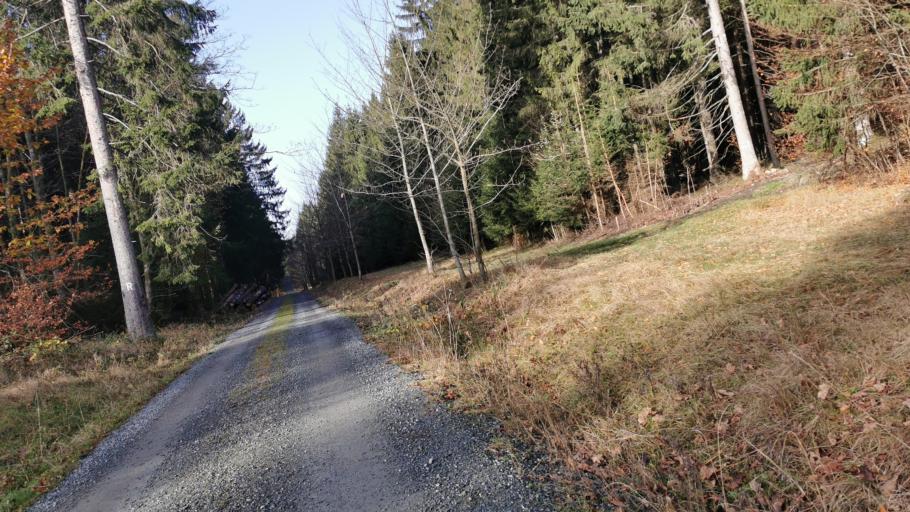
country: DE
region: Bavaria
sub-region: Upper Franconia
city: Reichenbach
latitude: 50.4409
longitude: 11.4480
